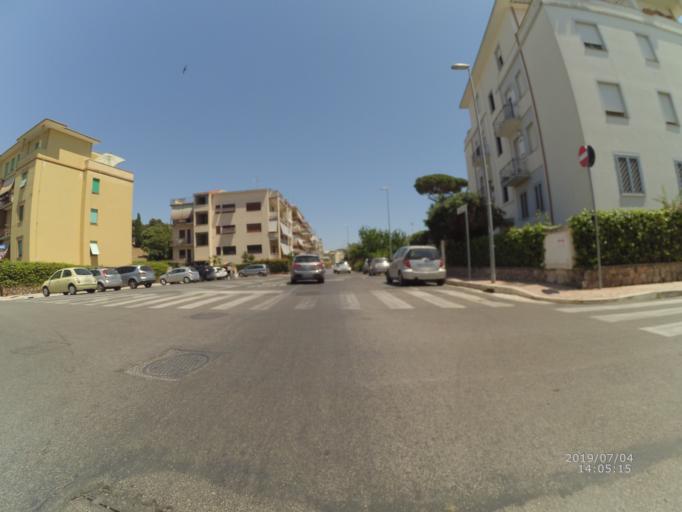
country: IT
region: Latium
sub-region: Provincia di Latina
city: Terracina
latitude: 41.2851
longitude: 13.2497
